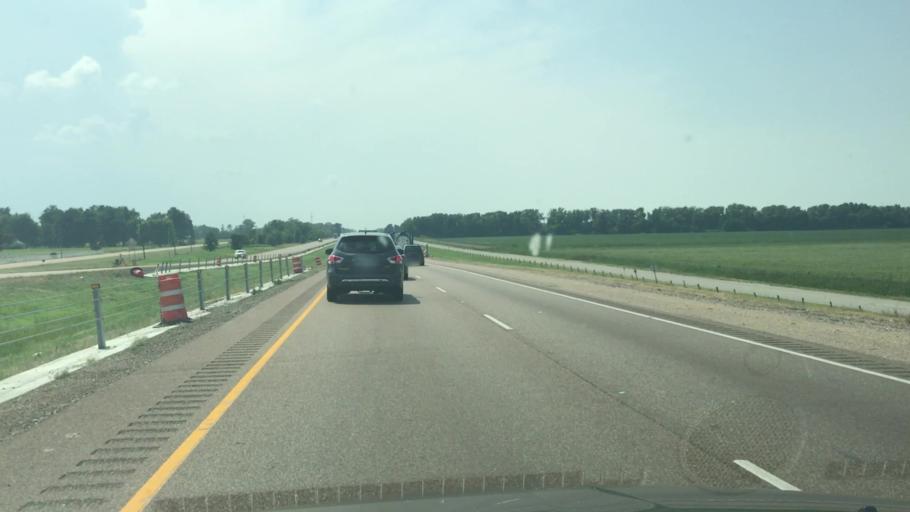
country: US
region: Arkansas
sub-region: Crittenden County
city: West Memphis
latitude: 35.1483
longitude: -90.3294
